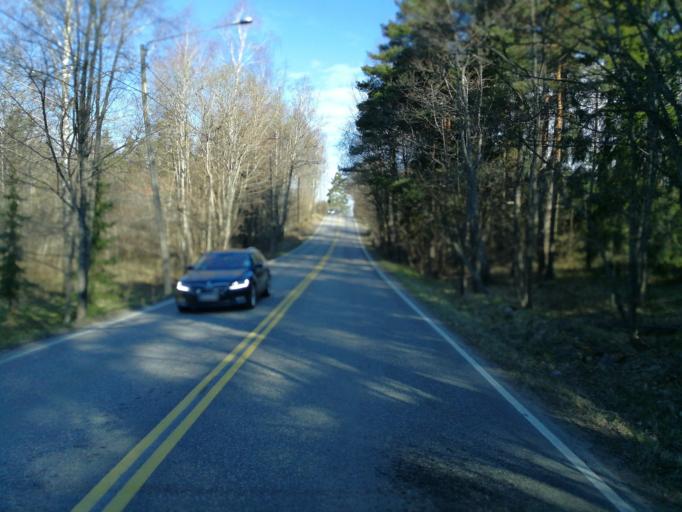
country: FI
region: Uusimaa
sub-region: Helsinki
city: Kirkkonummi
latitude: 60.2167
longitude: 24.4774
